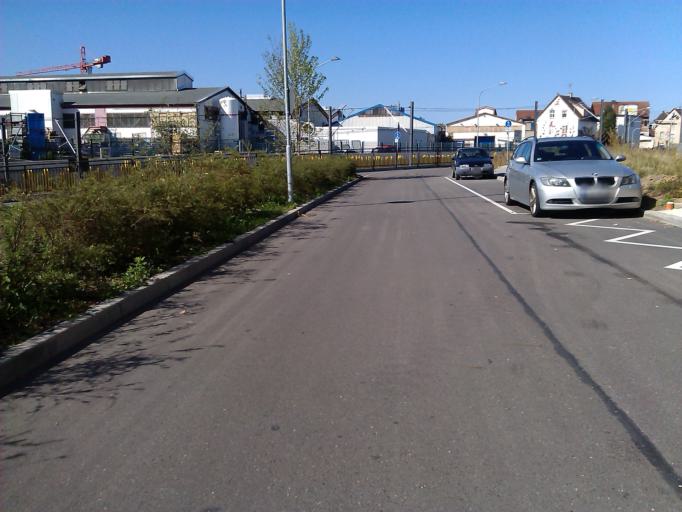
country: DE
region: Baden-Wuerttemberg
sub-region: Regierungsbezirk Stuttgart
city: Heilbronn
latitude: 49.1522
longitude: 9.2205
